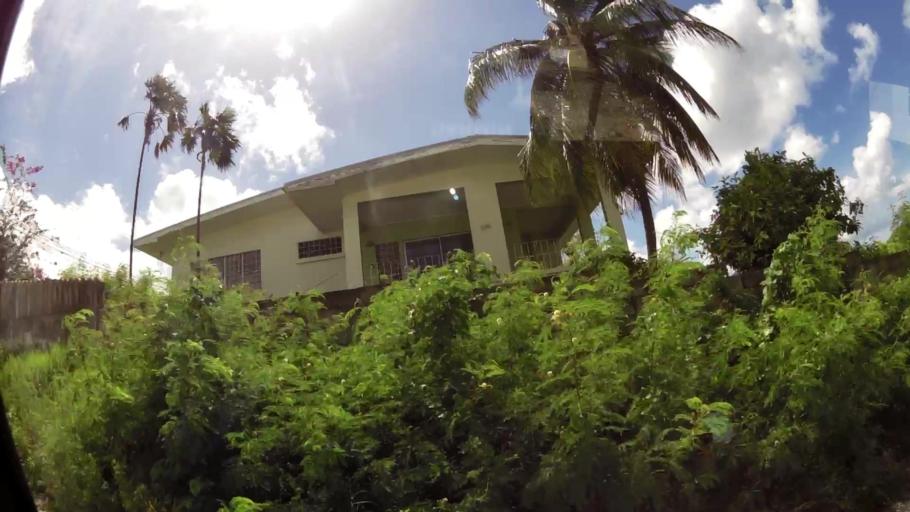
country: BB
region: Saint James
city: Holetown
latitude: 13.1559
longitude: -59.6351
